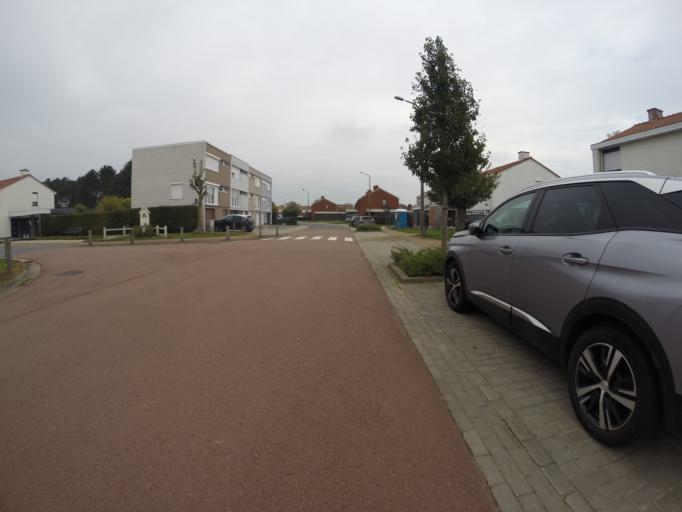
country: BE
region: Flanders
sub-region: Provincie West-Vlaanderen
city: Beernem
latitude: 51.1255
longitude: 3.3636
